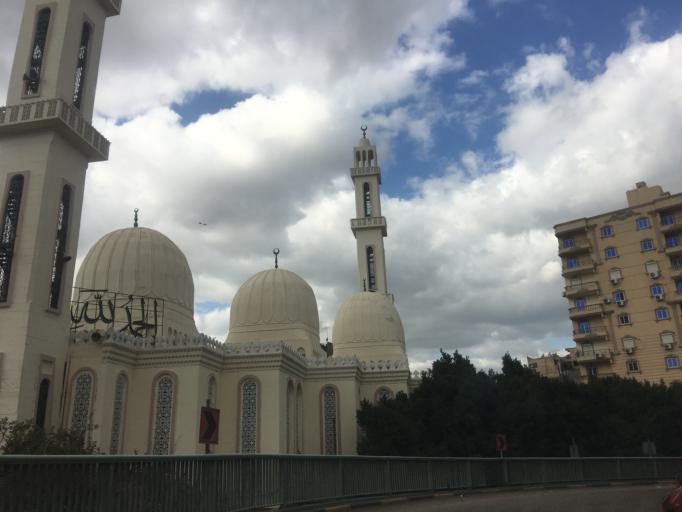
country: EG
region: Muhafazat al Qahirah
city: Cairo
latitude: 30.0483
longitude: 31.2167
